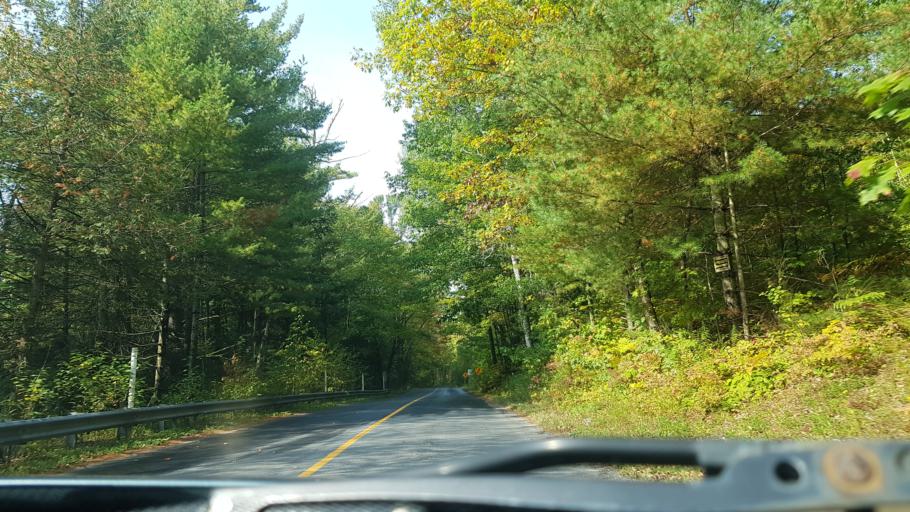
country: CA
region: Ontario
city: Gravenhurst
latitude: 44.7904
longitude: -79.2209
